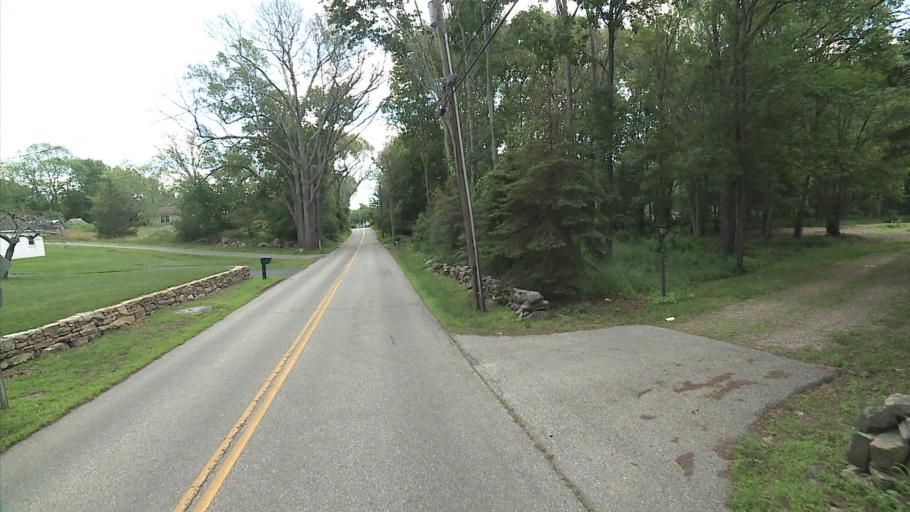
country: US
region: Connecticut
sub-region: New London County
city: Old Mystic
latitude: 41.4433
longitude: -71.8958
